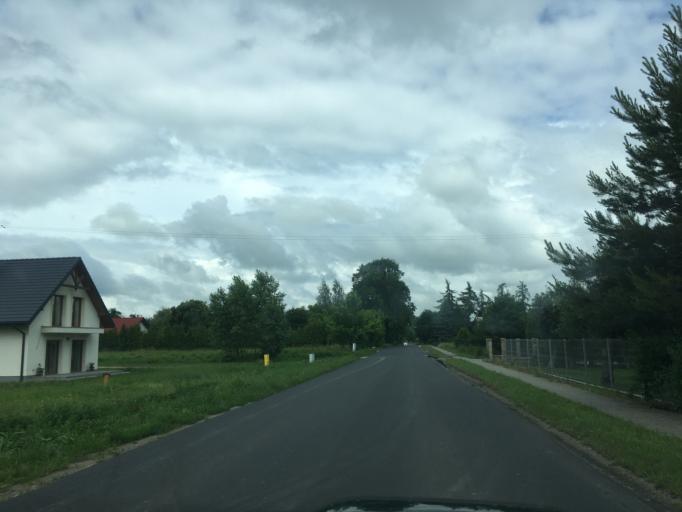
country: PL
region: Lublin Voivodeship
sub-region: Powiat swidnicki
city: Melgiew
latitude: 51.2155
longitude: 22.7510
